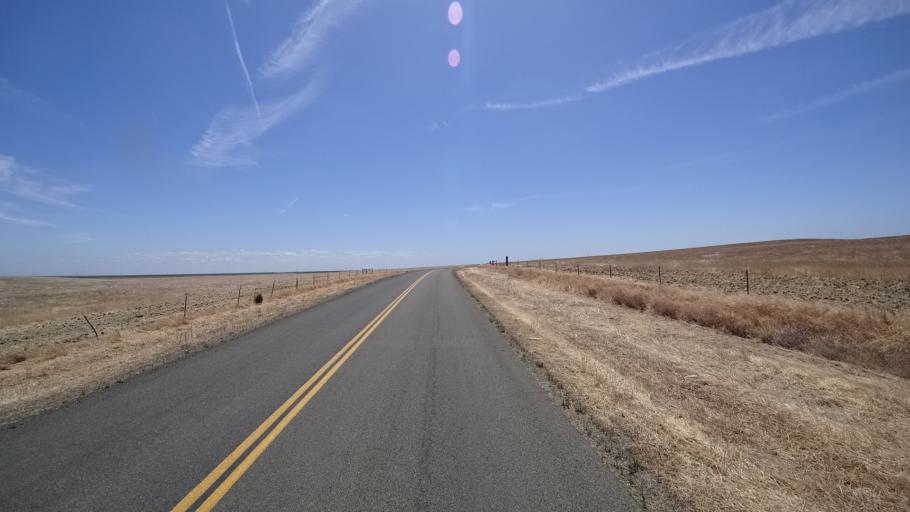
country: US
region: California
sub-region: Kings County
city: Kettleman City
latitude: 35.8099
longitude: -119.8996
